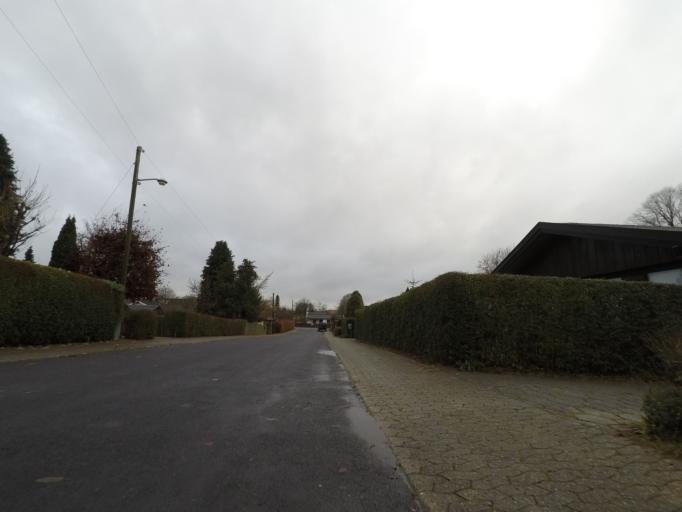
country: DK
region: Capital Region
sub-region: Ballerup Kommune
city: Ballerup
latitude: 55.7482
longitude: 12.3876
